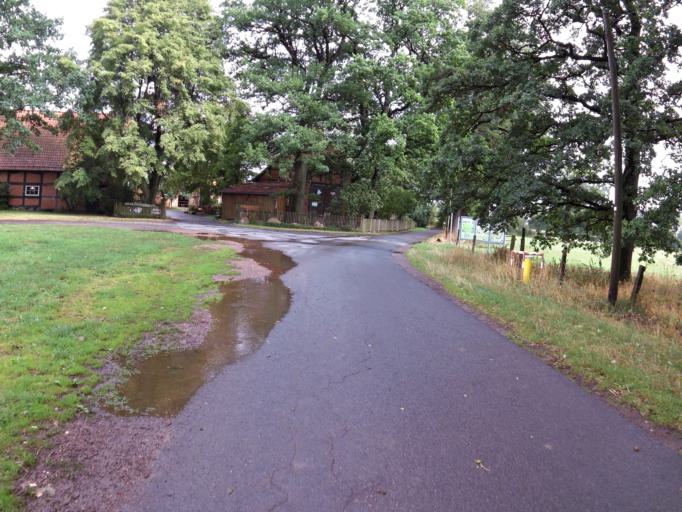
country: DE
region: Lower Saxony
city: Marklohe
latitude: 52.6793
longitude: 9.1716
